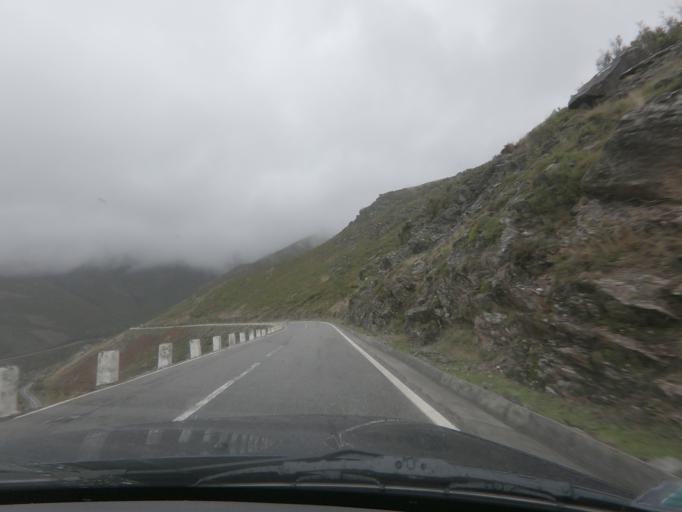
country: PT
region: Vila Real
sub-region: Mondim de Basto
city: Mondim de Basto
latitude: 41.3378
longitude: -7.8740
